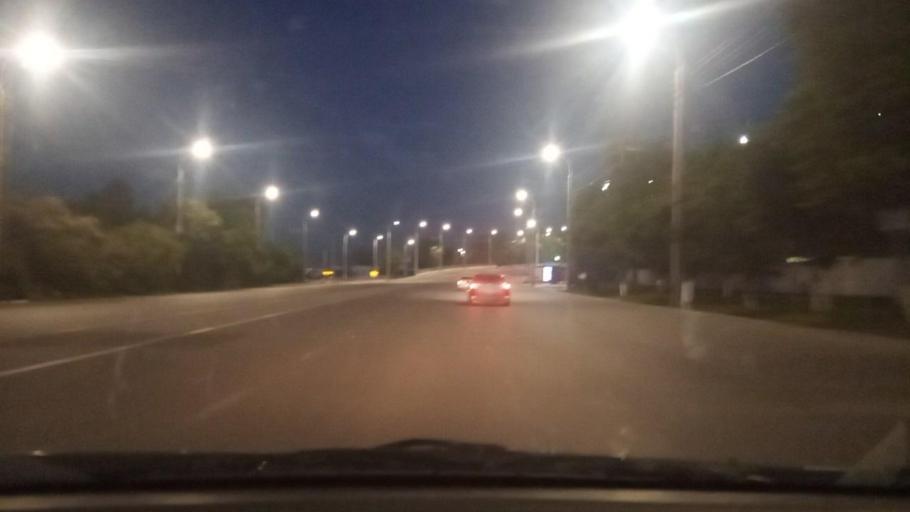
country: UZ
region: Toshkent Shahri
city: Tashkent
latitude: 41.2619
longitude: 69.2310
